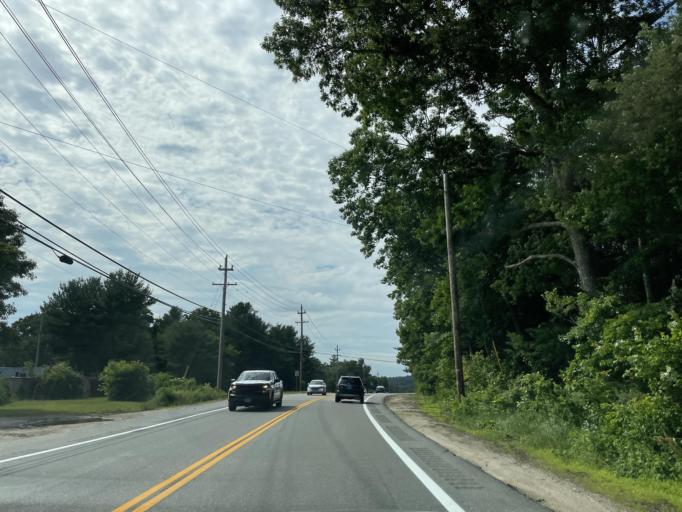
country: US
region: Rhode Island
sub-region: Kent County
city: West Greenwich
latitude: 41.5985
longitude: -71.6526
